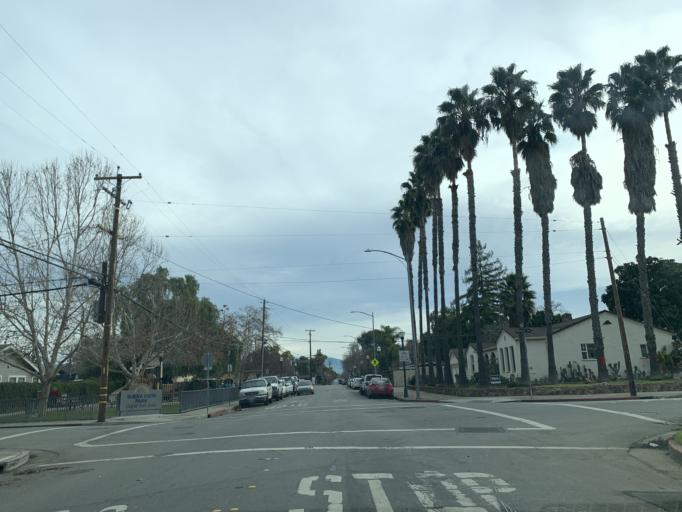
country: US
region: California
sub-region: Santa Clara County
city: Buena Vista
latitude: 37.3197
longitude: -121.9220
